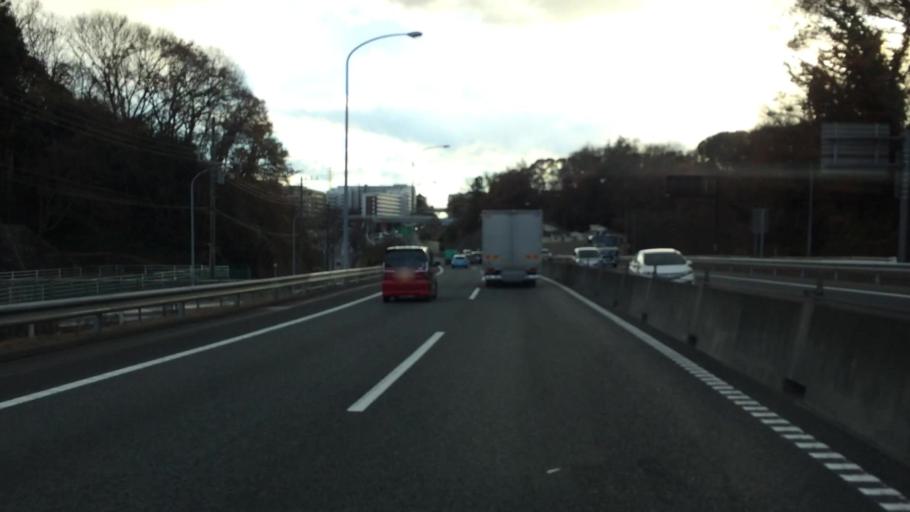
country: JP
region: Kanagawa
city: Yokohama
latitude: 35.4386
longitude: 139.5559
